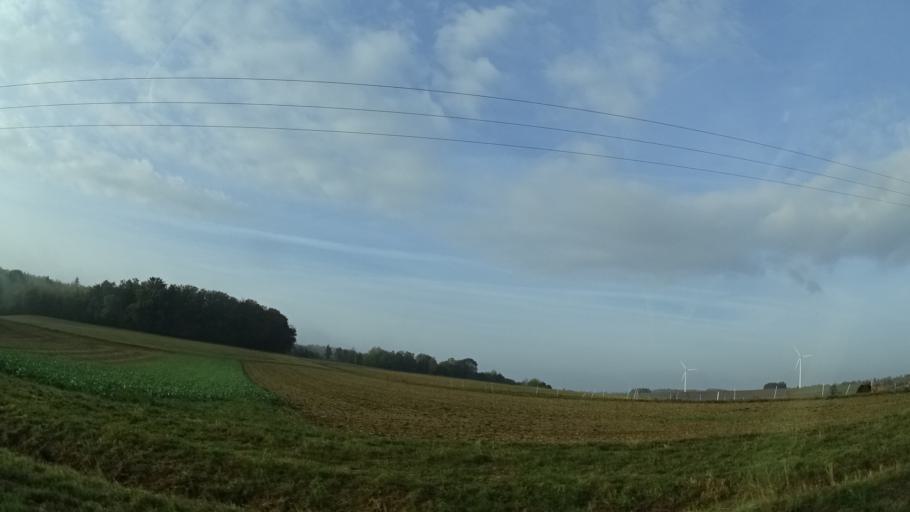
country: DE
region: Hesse
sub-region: Regierungsbezirk Darmstadt
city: Hirzenhain
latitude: 50.4146
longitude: 9.1380
